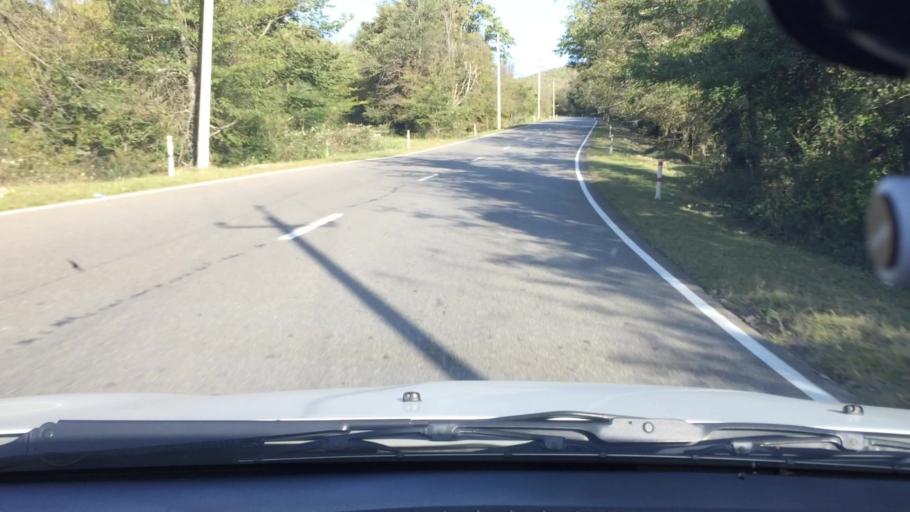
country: GE
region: Imereti
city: Kutaisi
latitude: 42.2477
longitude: 42.7561
